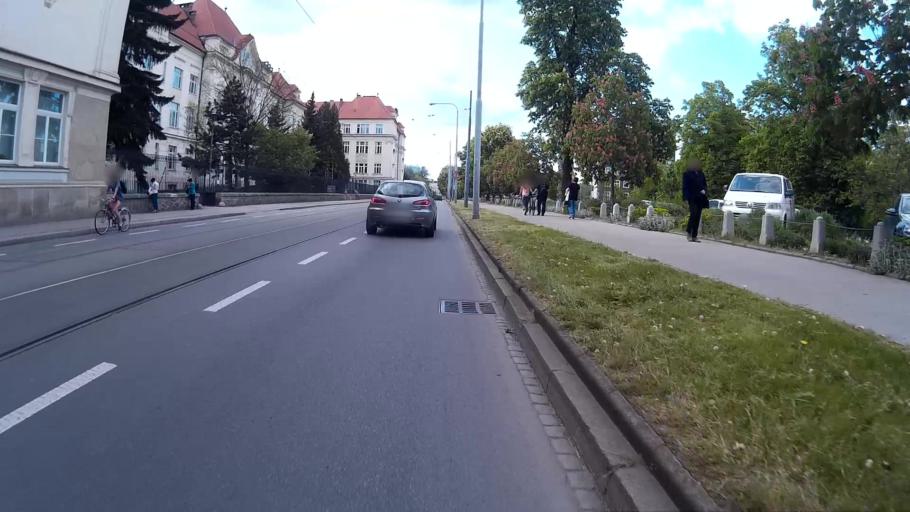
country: CZ
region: South Moravian
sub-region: Mesto Brno
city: Brno
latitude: 49.2064
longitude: 16.5932
